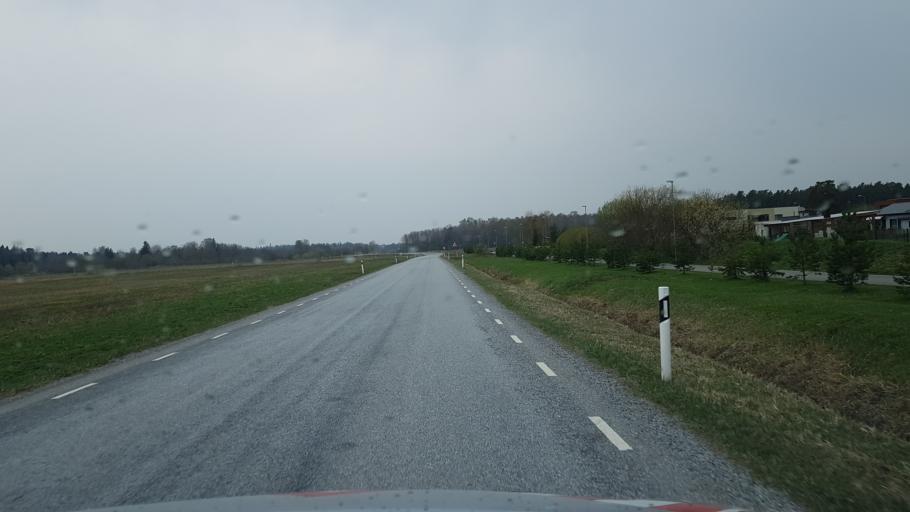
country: EE
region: Harju
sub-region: Saue vald
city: Laagri
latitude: 59.3427
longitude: 24.5915
